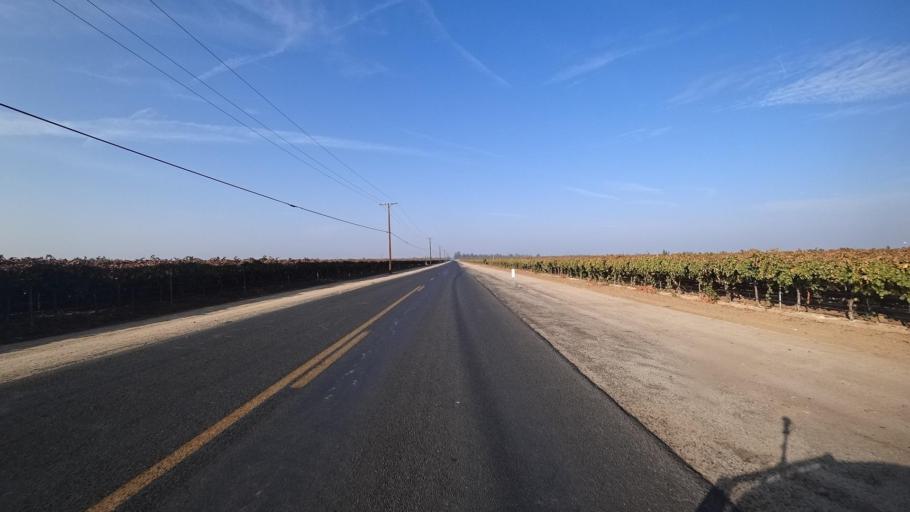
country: US
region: California
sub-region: Kern County
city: McFarland
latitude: 35.6746
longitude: -119.1987
